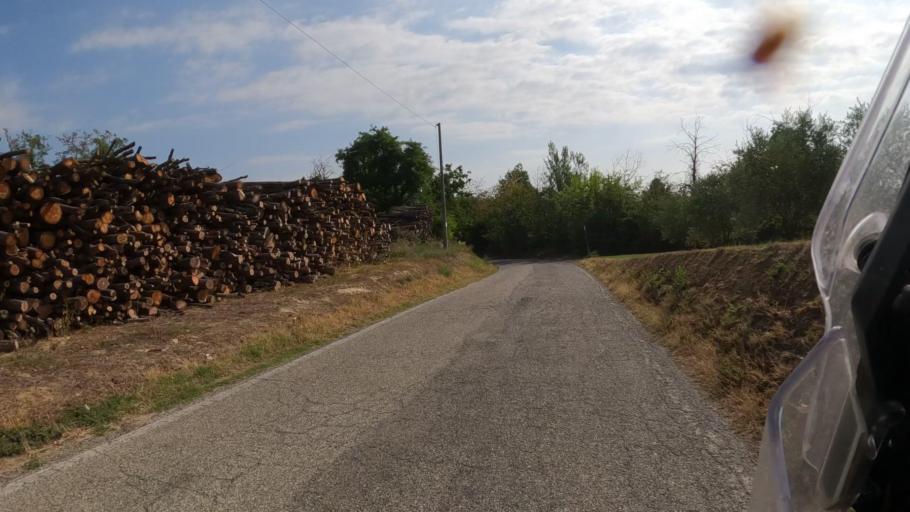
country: IT
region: Piedmont
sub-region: Provincia di Alessandria
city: Altavilla Monferrato
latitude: 44.9665
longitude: 8.3844
